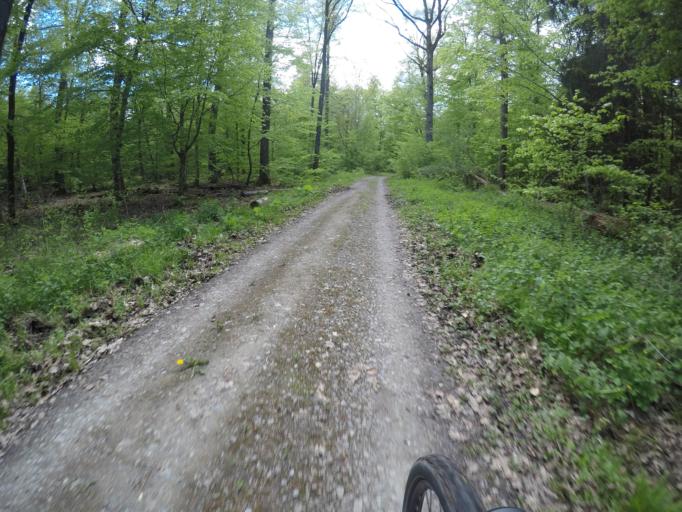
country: DE
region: Baden-Wuerttemberg
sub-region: Regierungsbezirk Stuttgart
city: Nufringen
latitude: 48.5937
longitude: 8.9215
